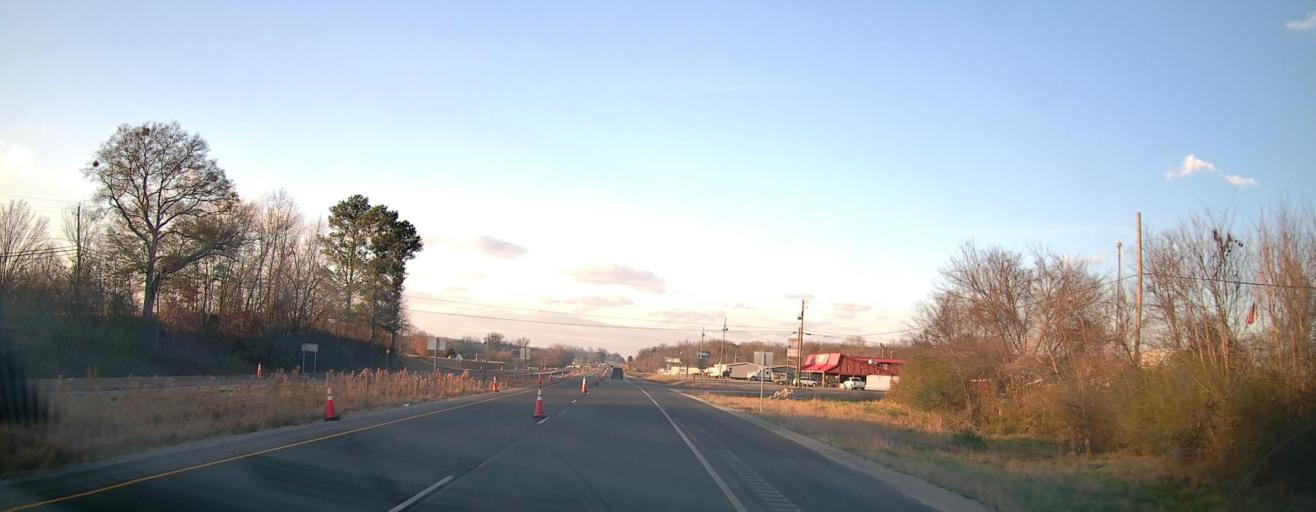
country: US
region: Alabama
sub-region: Calhoun County
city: Alexandria
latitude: 33.7306
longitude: -85.8786
